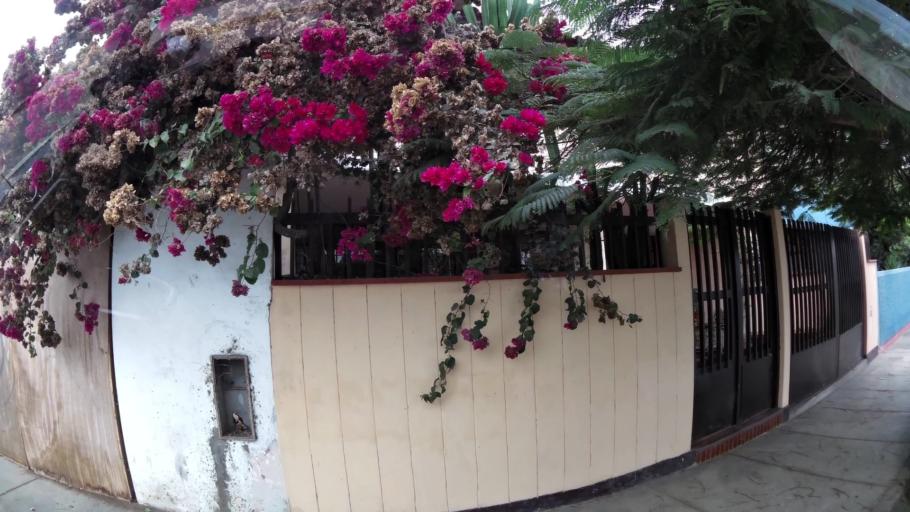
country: PE
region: Lima
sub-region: Lima
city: Surco
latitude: -12.1594
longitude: -77.0246
